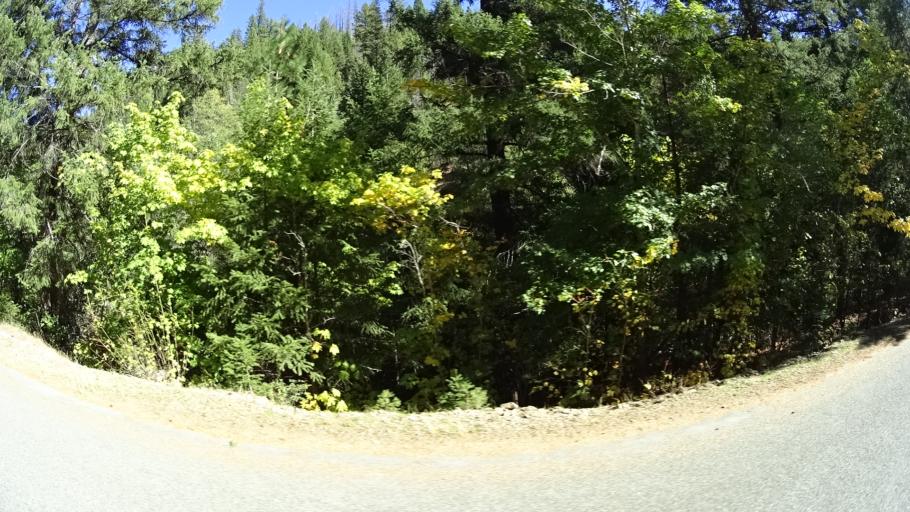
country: US
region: California
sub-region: Siskiyou County
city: Happy Camp
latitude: 41.3394
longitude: -123.0459
